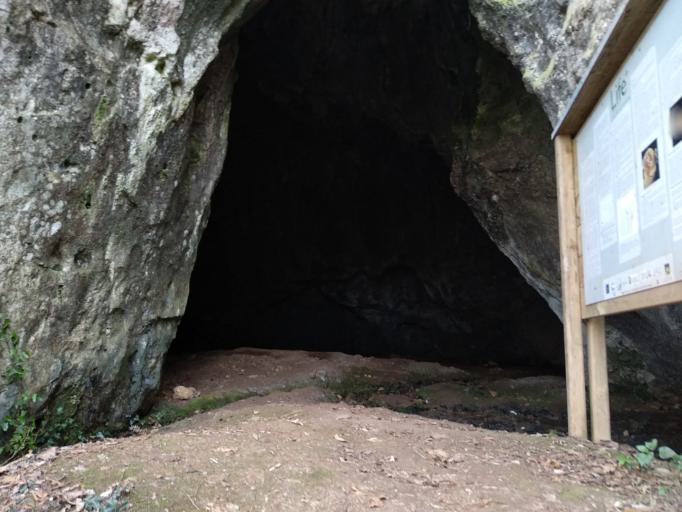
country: IT
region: Veneto
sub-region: Provincia di Vicenza
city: Lumignano
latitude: 45.4551
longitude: 11.5776
